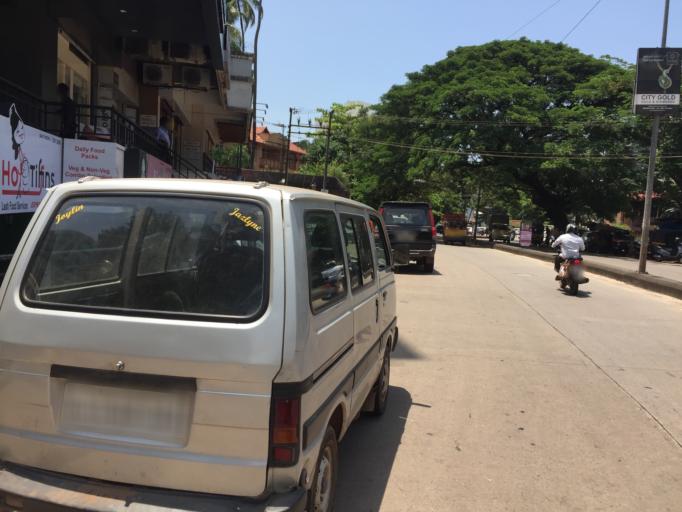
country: IN
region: Karnataka
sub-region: Dakshina Kannada
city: Mangalore
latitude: 12.8784
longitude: 74.8511
